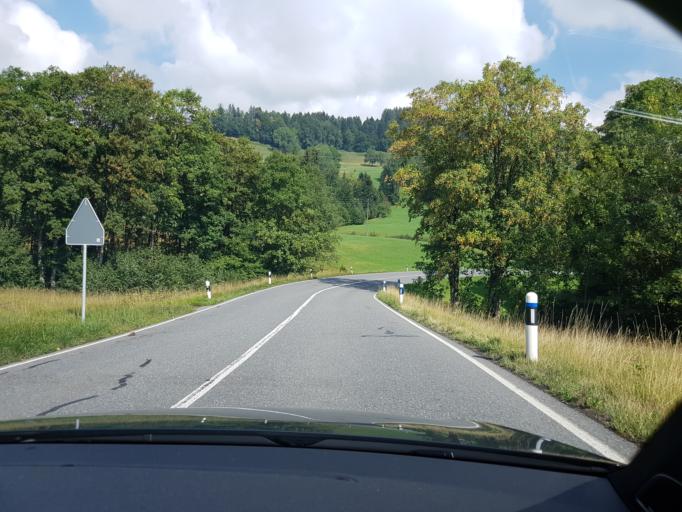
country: CH
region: Saint Gallen
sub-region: Wahlkreis Toggenburg
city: Wattwil
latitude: 47.2706
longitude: 9.0548
